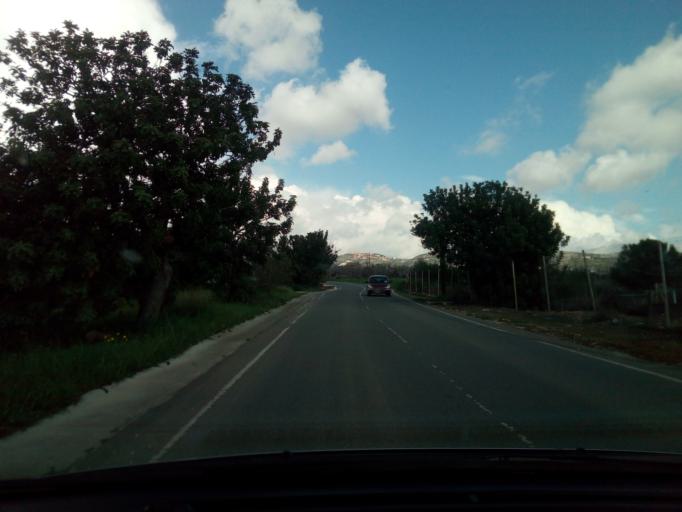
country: CY
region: Pafos
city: Mesogi
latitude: 34.8090
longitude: 32.4423
